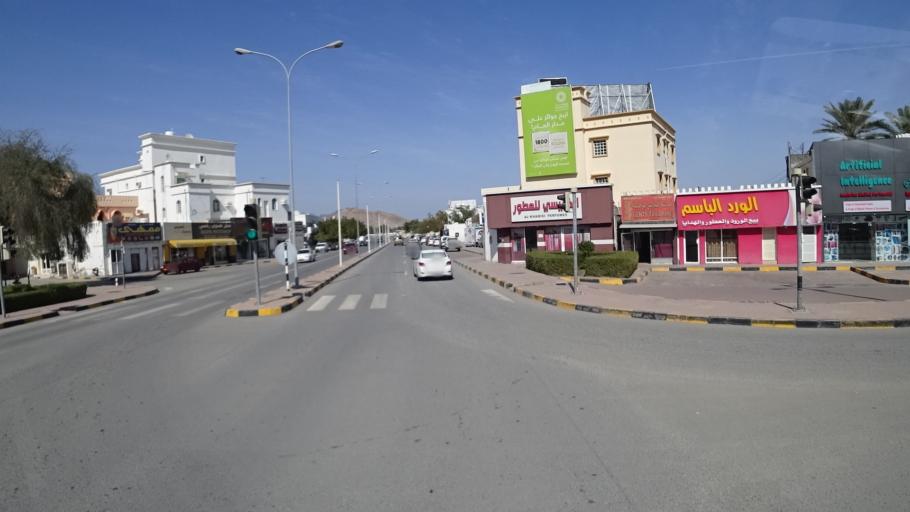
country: OM
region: Al Batinah
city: Rustaq
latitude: 23.3916
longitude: 57.4230
